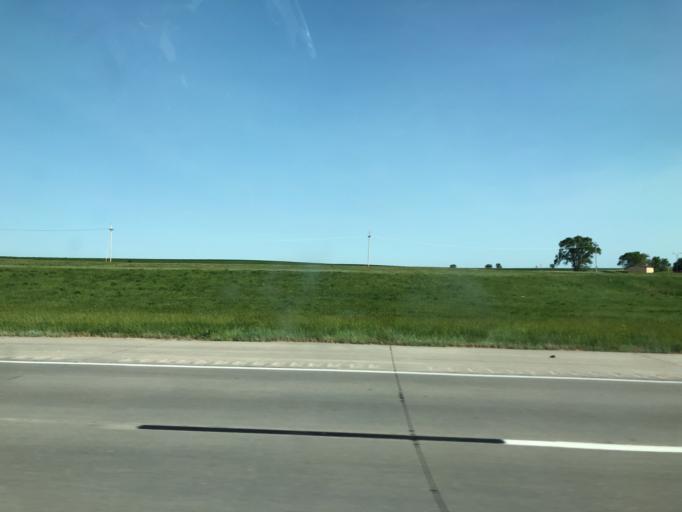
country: US
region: Nebraska
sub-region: Saunders County
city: Ashland
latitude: 40.9716
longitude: -96.3883
